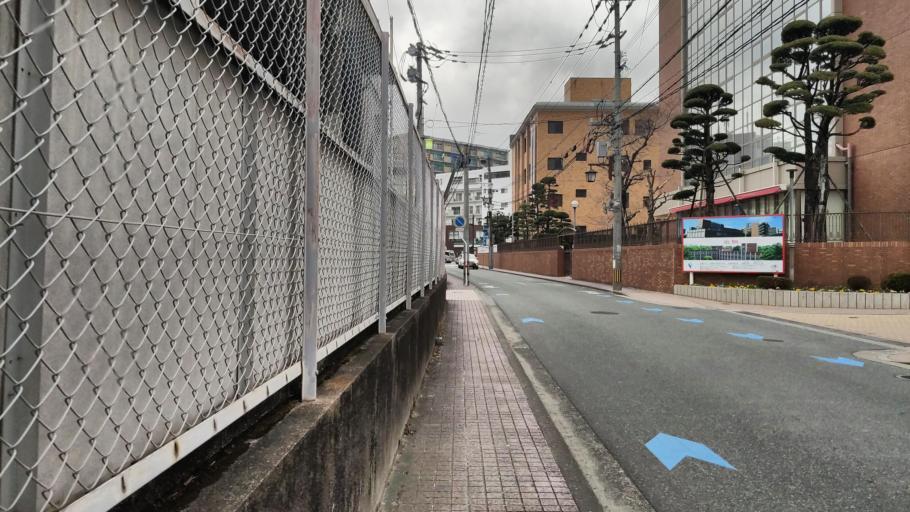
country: JP
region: Kumamoto
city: Kumamoto
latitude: 32.7973
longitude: 130.7162
